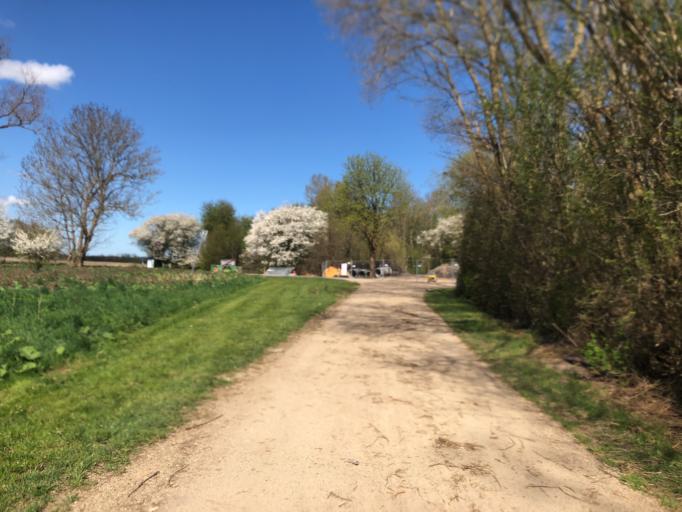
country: DK
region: Zealand
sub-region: Ringsted Kommune
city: Ringsted
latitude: 55.4431
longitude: 11.7766
